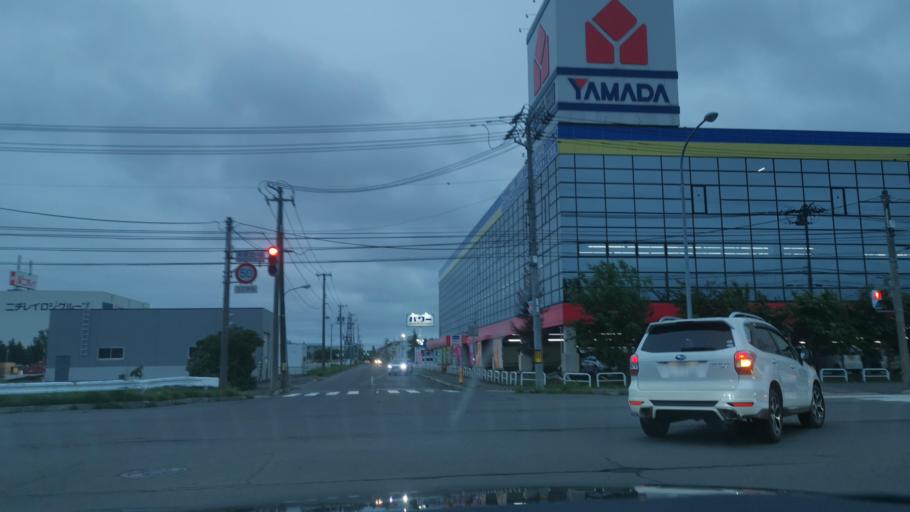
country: JP
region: Hokkaido
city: Sapporo
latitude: 43.1062
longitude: 141.2745
